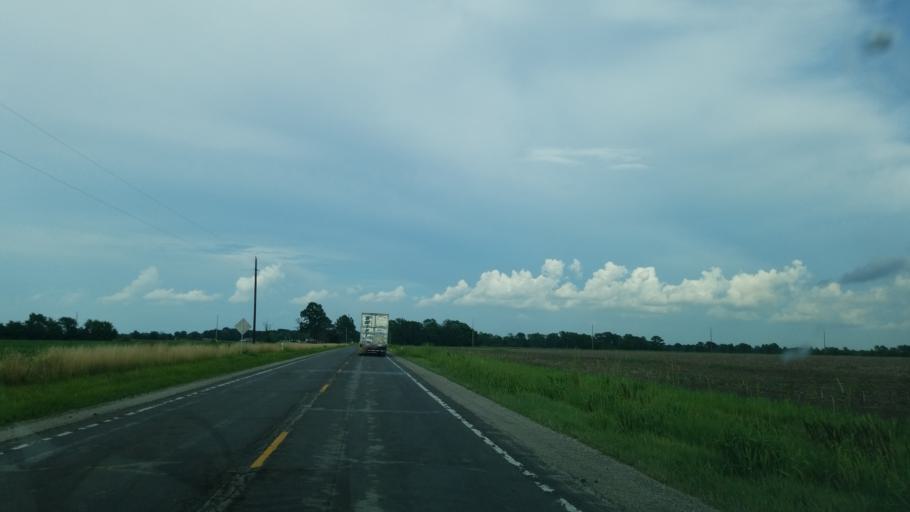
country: US
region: Illinois
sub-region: Marion County
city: Sandoval
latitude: 38.6166
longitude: -89.1458
